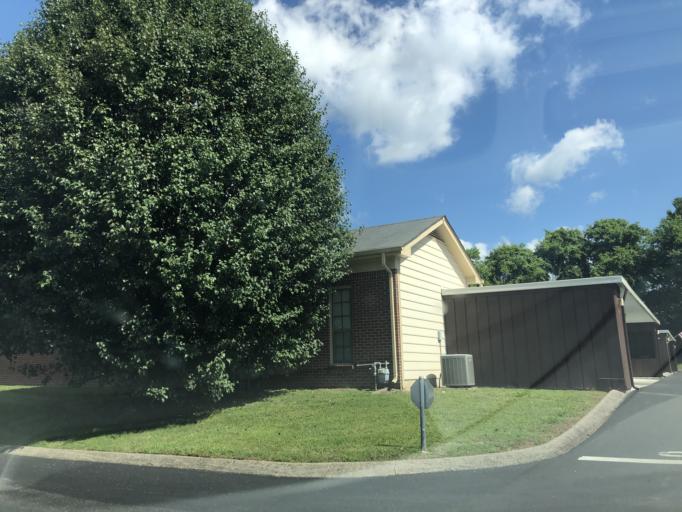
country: US
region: Tennessee
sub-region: Davidson County
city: Belle Meade
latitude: 36.0655
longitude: -86.9493
